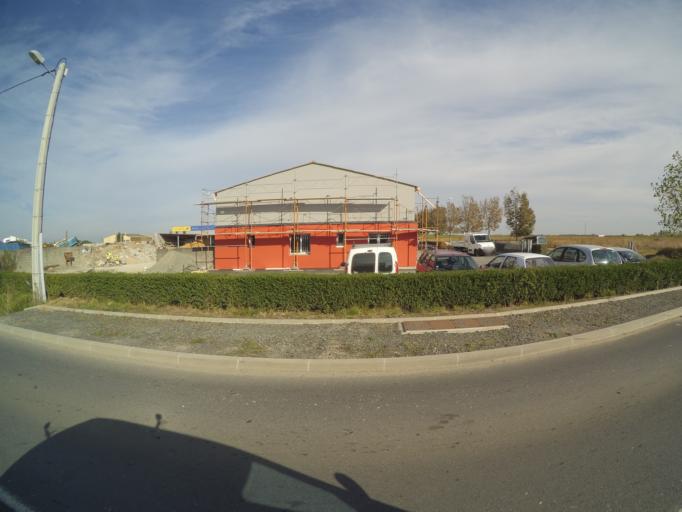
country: FR
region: Pays de la Loire
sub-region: Departement de la Loire-Atlantique
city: Mouzillon
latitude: 47.1263
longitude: -1.2795
